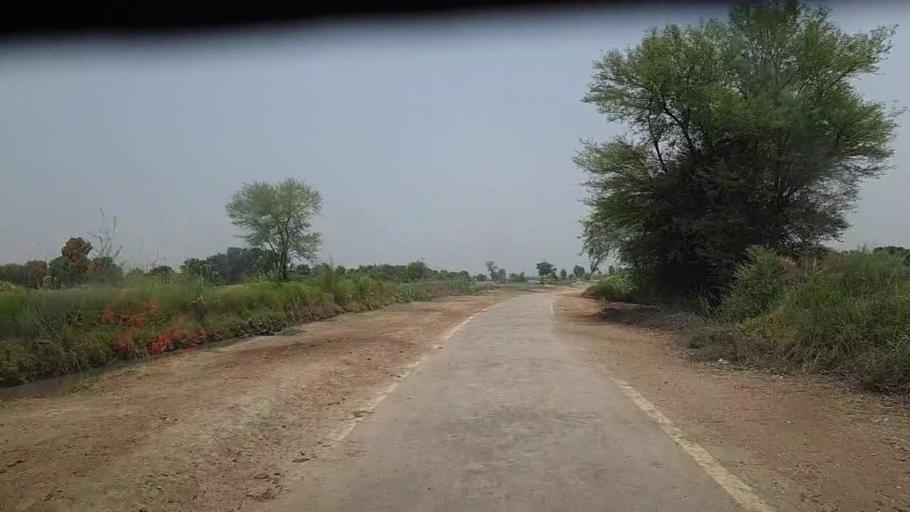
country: PK
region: Sindh
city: Sita Road
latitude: 27.0415
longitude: 67.9013
